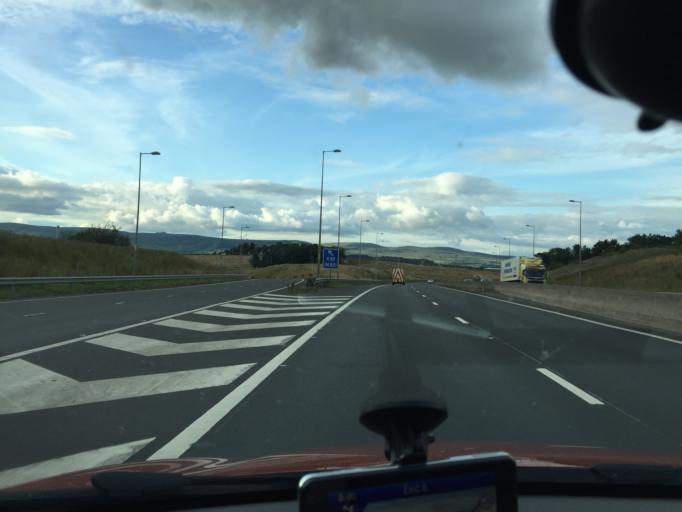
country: GB
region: Scotland
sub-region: North Lanarkshire
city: Glenboig
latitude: 55.9143
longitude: -4.0654
